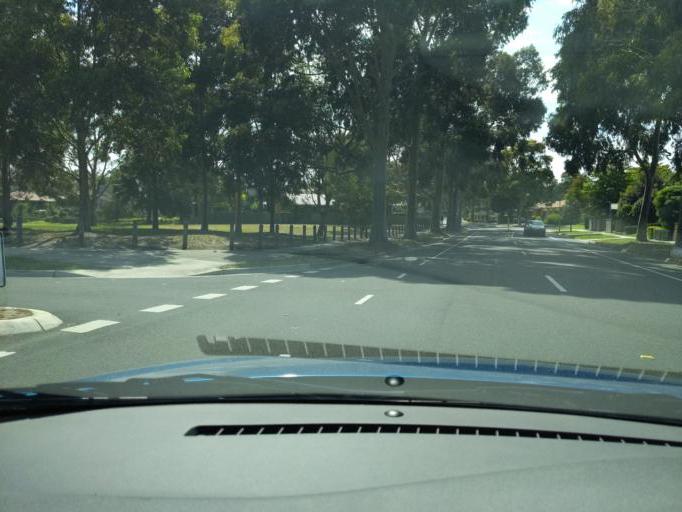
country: AU
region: Victoria
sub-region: Knox
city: Scoresby
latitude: -37.9161
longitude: 145.2428
